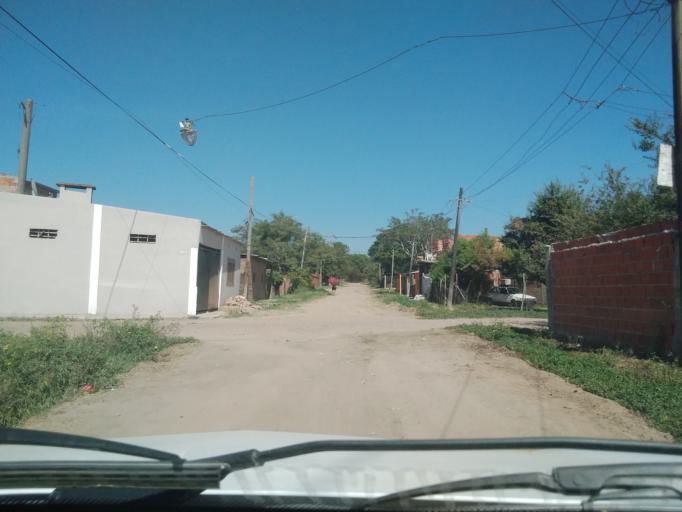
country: AR
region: Corrientes
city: Corrientes
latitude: -27.5118
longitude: -58.8036
